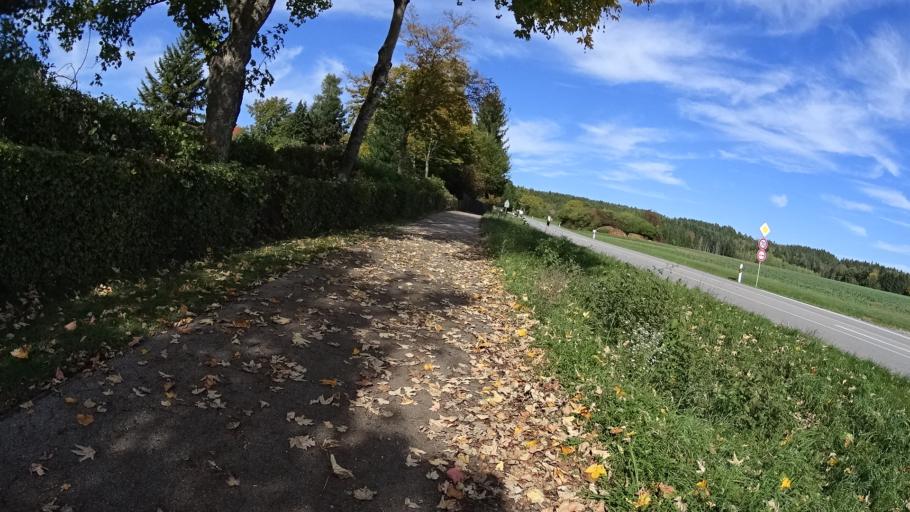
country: DE
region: Bavaria
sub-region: Upper Bavaria
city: Gaimersheim
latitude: 48.8369
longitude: 11.3696
